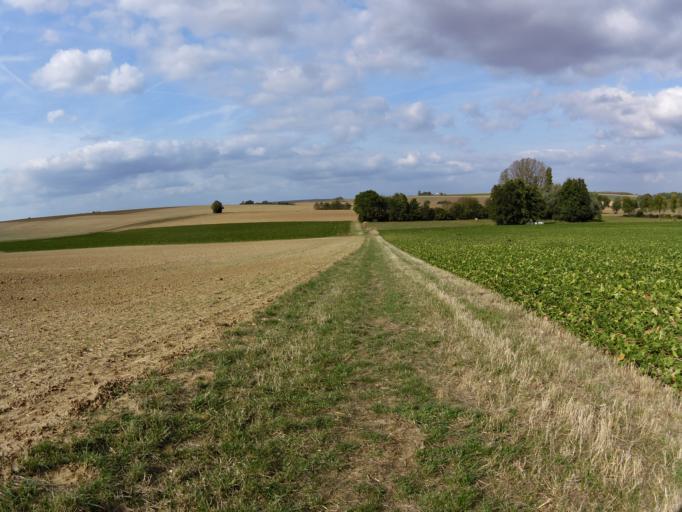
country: DE
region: Bavaria
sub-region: Regierungsbezirk Unterfranken
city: Giebelstadt
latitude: 49.6977
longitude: 9.9494
